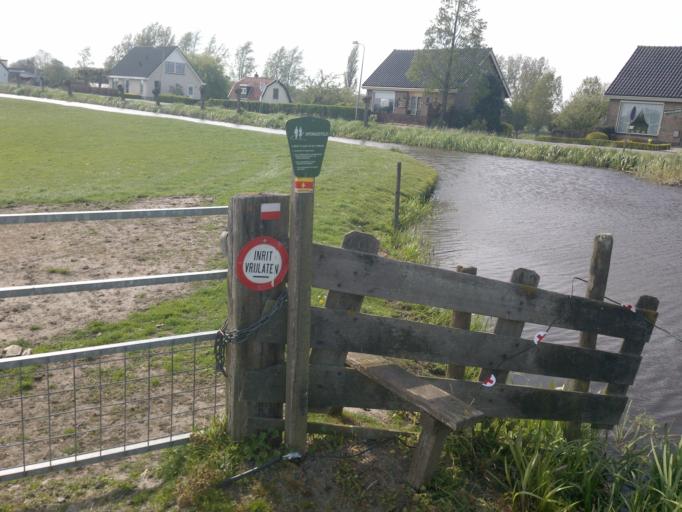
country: NL
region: South Holland
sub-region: Gemeente Nieuwkoop
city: Nieuwkoop
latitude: 52.2036
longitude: 4.7685
